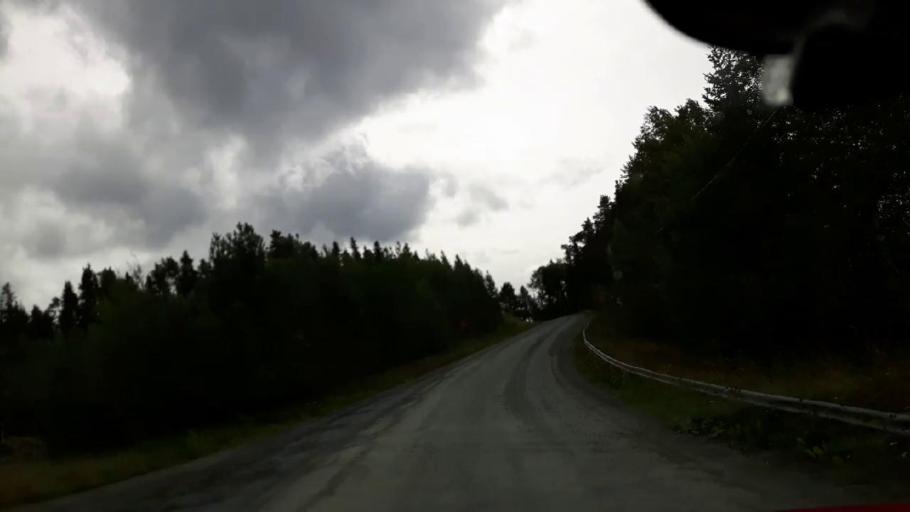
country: SE
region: Jaemtland
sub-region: Krokoms Kommun
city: Krokom
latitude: 63.5707
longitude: 14.2405
